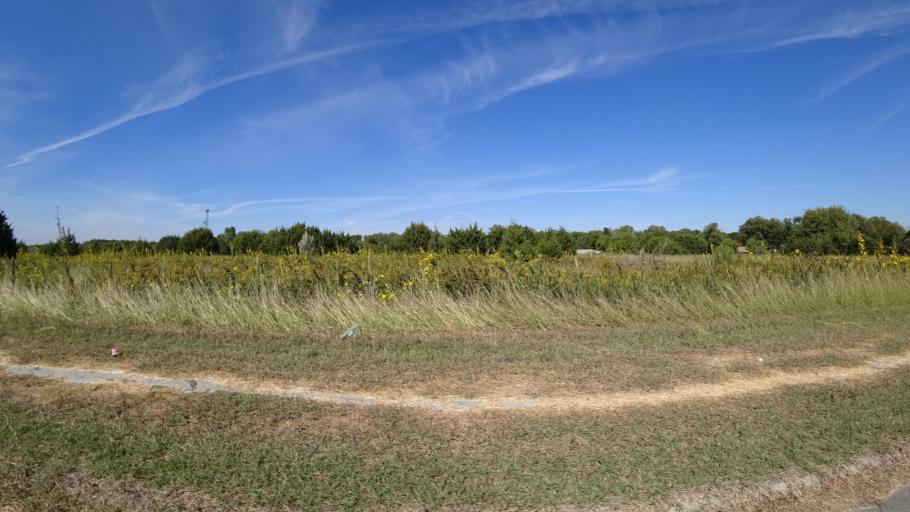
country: US
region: Texas
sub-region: Travis County
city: Austin
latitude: 30.1898
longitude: -97.7016
